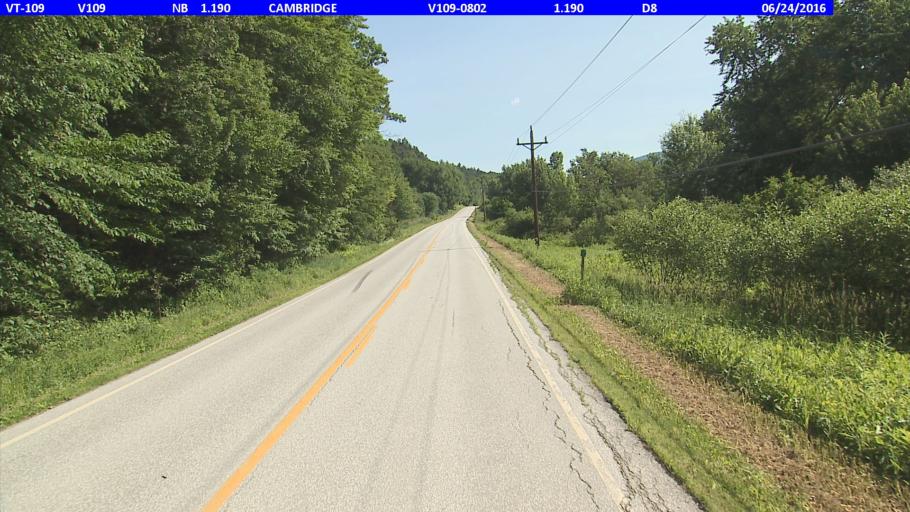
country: US
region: Vermont
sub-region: Lamoille County
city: Johnson
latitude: 44.6580
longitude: -72.8083
